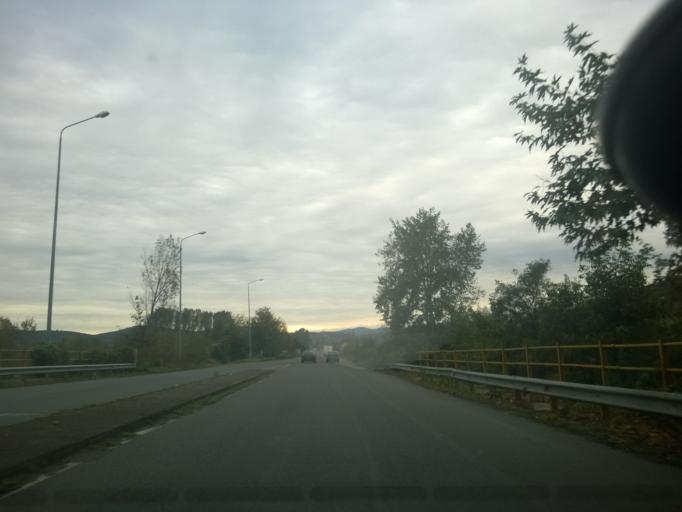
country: GR
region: Central Macedonia
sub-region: Nomos Pellis
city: Aridaia
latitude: 40.9404
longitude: 22.0838
